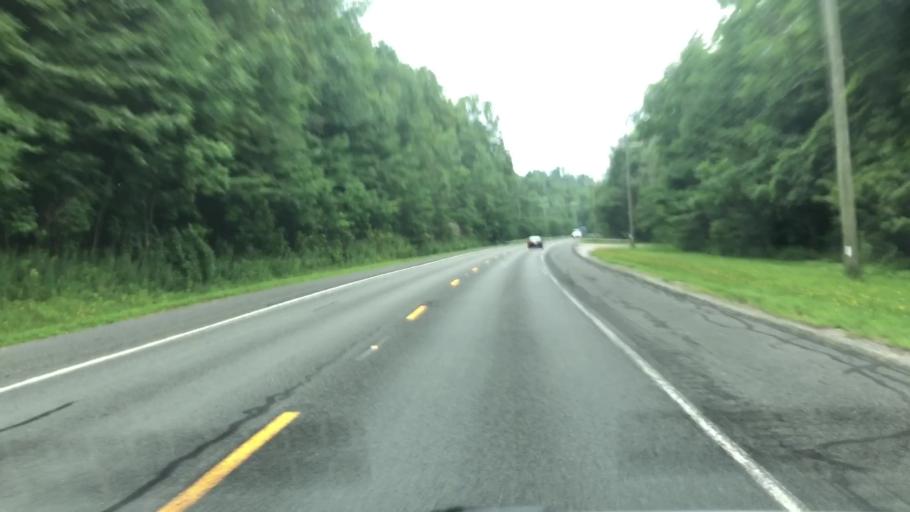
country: US
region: Massachusetts
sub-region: Berkshire County
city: Lanesborough
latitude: 42.5488
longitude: -73.2338
